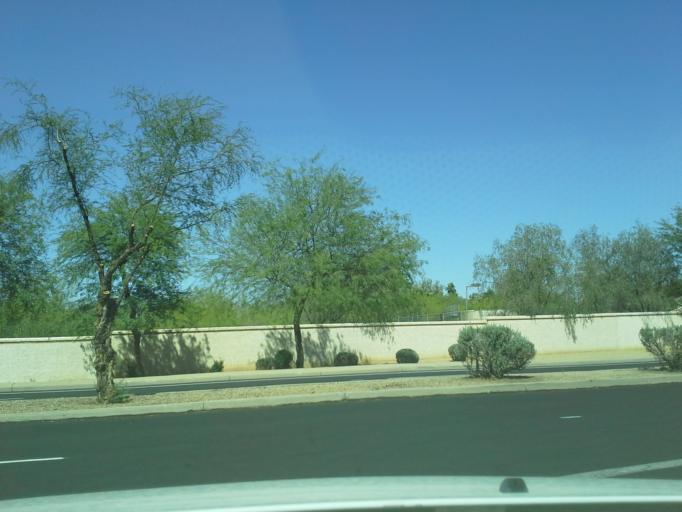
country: US
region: Arizona
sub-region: Maricopa County
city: Paradise Valley
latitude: 33.5855
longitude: -111.9234
